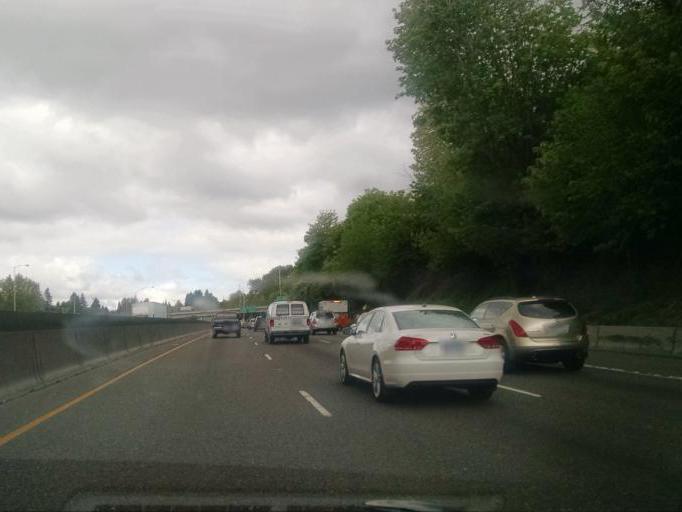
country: US
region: Oregon
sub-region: Clackamas County
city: Milwaukie
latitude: 45.4698
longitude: -122.6815
